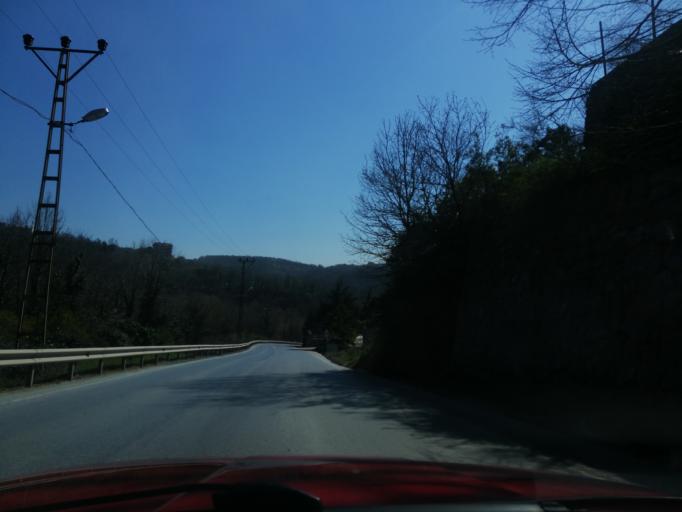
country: TR
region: Istanbul
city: Mahmut Sevket Pasa
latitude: 41.1019
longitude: 29.1588
